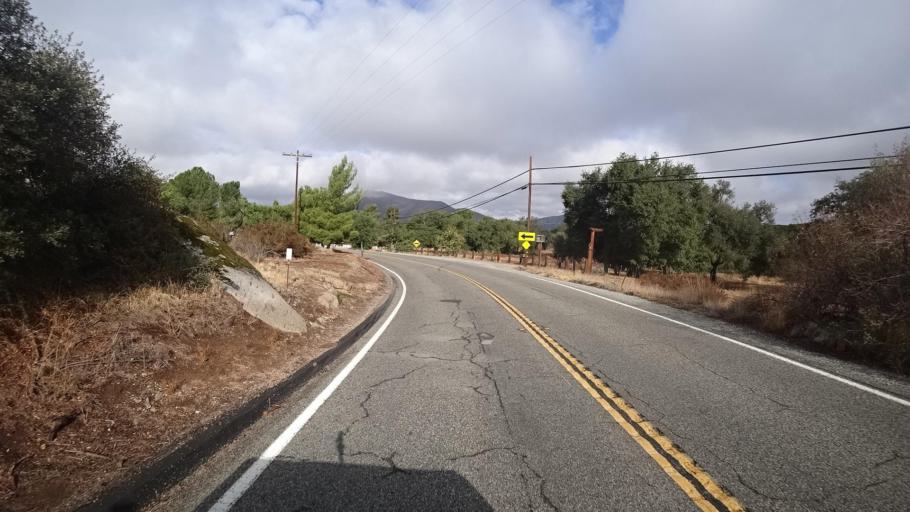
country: MX
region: Baja California
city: Tecate
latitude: 32.6039
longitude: -116.6071
